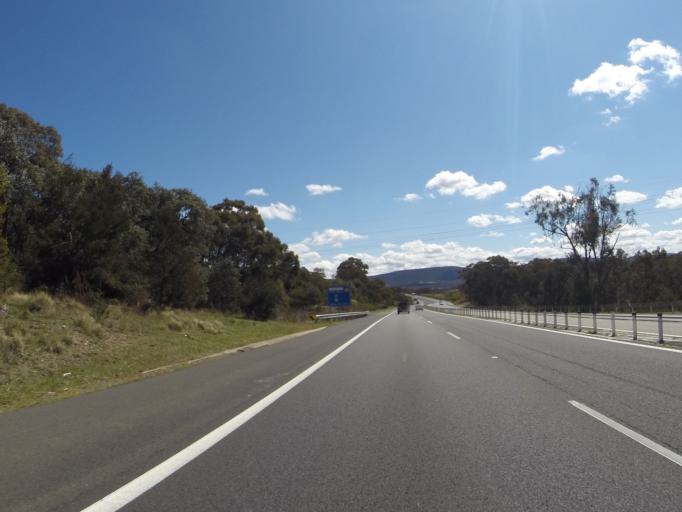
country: AU
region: New South Wales
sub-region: Goulburn Mulwaree
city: Goulburn
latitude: -34.7389
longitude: 149.8351
